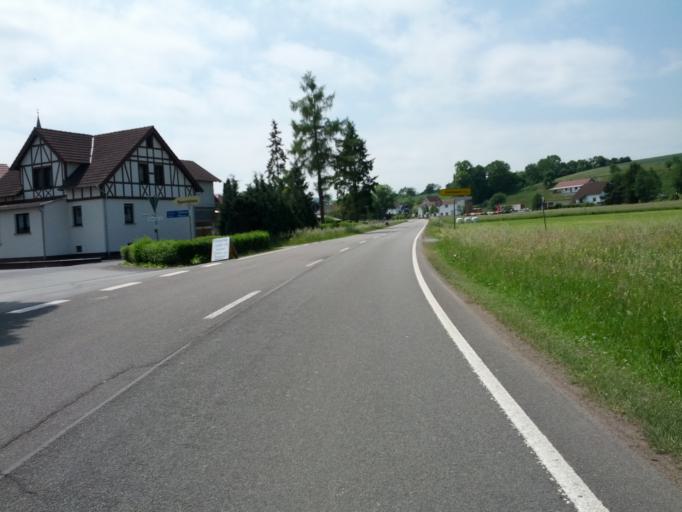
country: DE
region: Thuringia
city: Urnshausen
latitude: 50.7382
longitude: 10.1733
